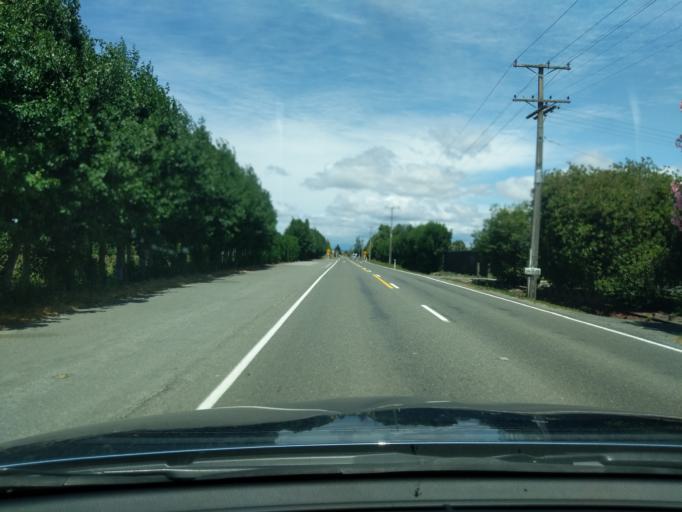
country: NZ
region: Tasman
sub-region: Tasman District
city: Motueka
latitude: -41.0881
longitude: 172.9968
